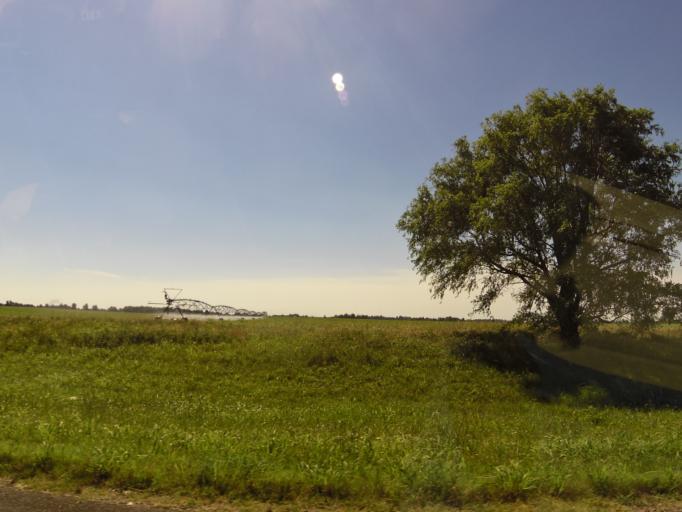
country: US
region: Missouri
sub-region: Dunklin County
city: Clarkton
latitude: 36.4969
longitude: -90.0036
